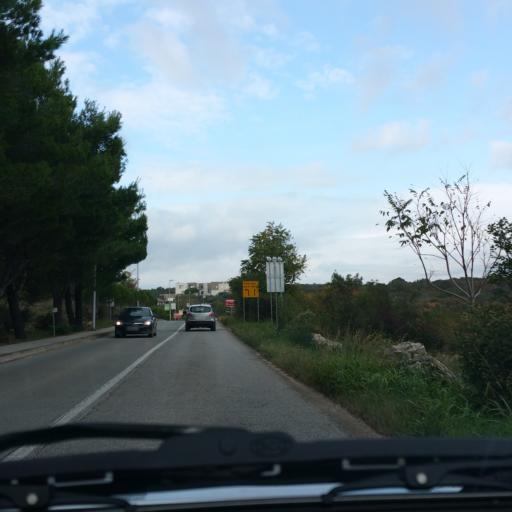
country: HR
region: Primorsko-Goranska
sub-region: Grad Krk
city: Krk
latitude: 45.0331
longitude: 14.5710
